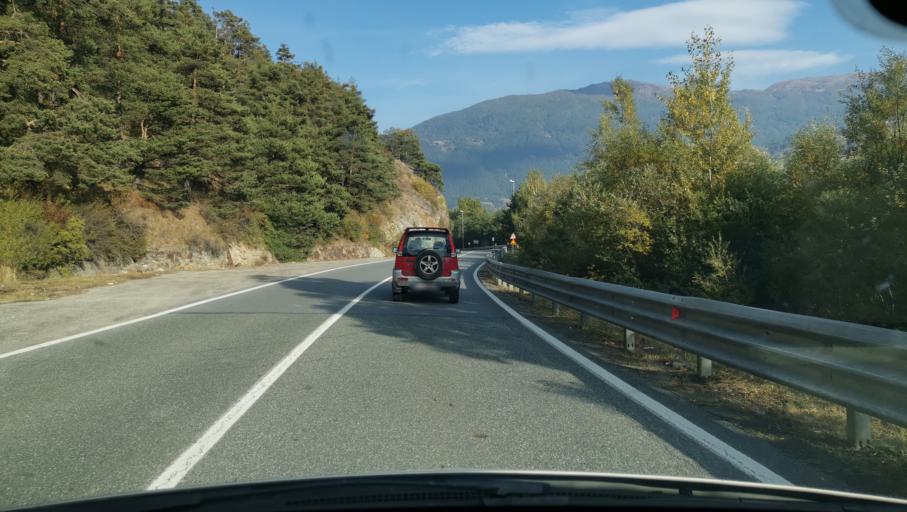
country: IT
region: Piedmont
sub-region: Provincia di Torino
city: Oulx
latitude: 45.0416
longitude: 6.8229
